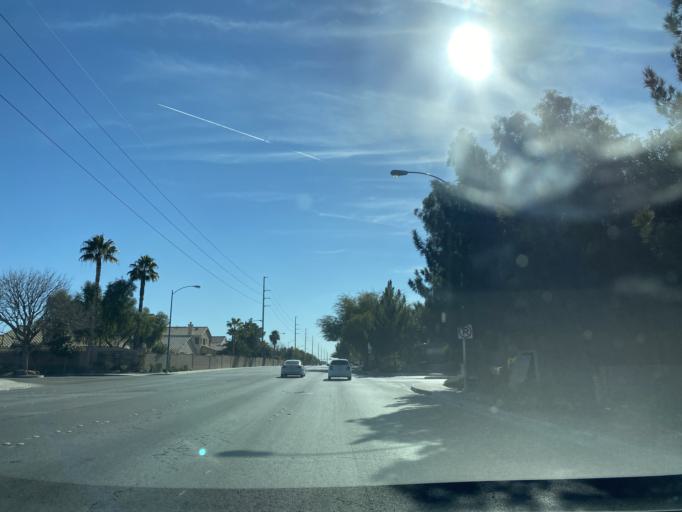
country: US
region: Nevada
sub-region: Clark County
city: North Las Vegas
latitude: 36.2382
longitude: -115.1437
